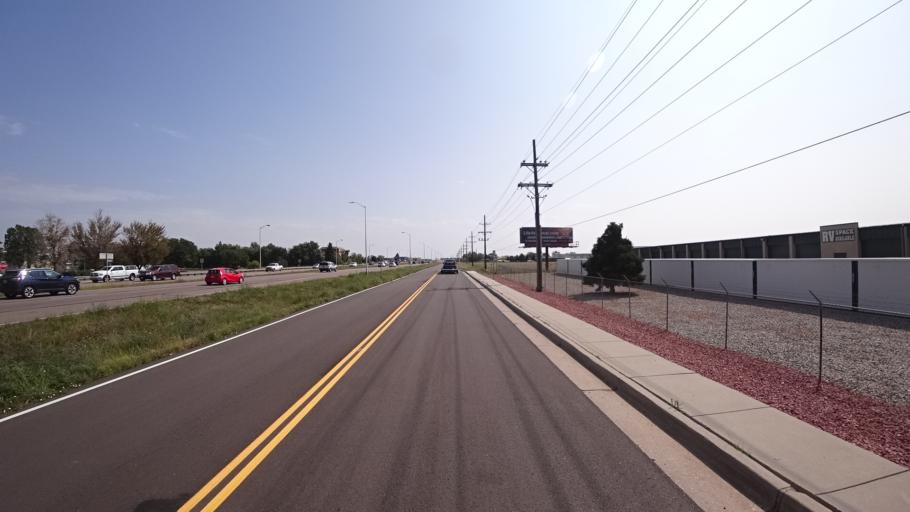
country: US
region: Colorado
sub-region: El Paso County
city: Cimarron Hills
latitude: 38.8395
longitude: -104.7371
